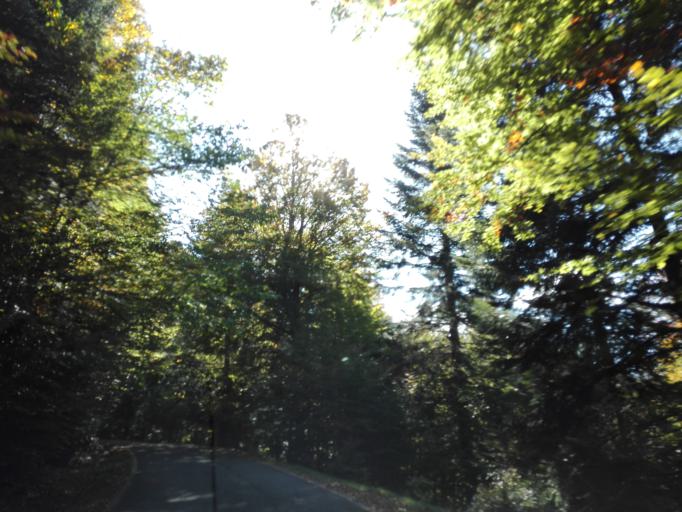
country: ES
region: Navarre
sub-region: Provincia de Navarra
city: Oronz
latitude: 42.9802
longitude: -1.1131
